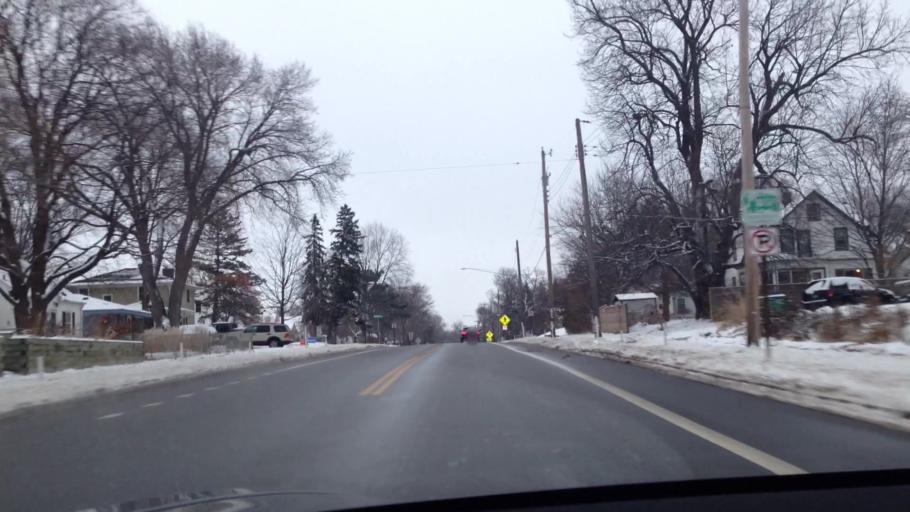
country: US
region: Minnesota
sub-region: Hennepin County
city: Saint Louis Park
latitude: 44.9495
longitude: -93.3569
